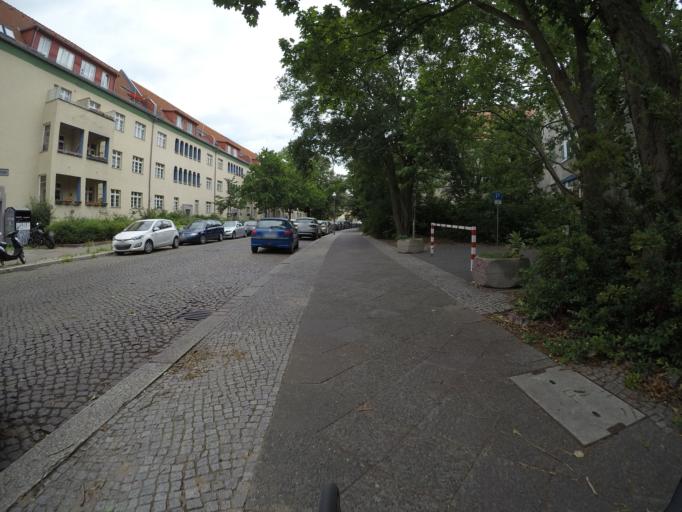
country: DE
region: Berlin
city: Wilhelmsruh
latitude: 52.5702
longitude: 13.3569
